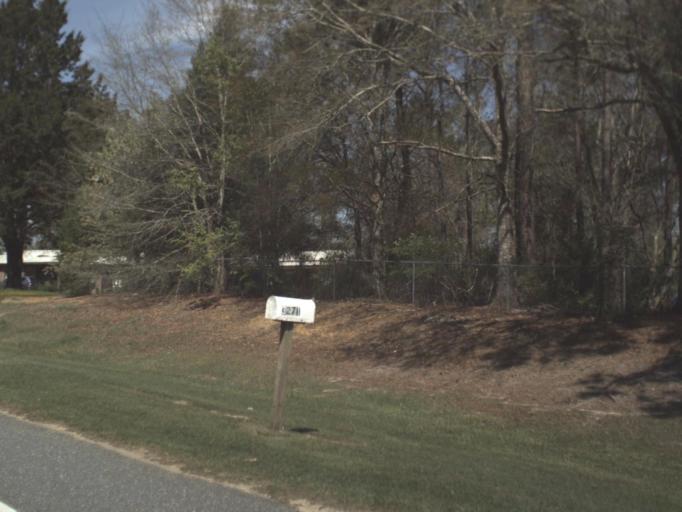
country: US
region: Florida
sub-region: Holmes County
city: Bonifay
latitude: 30.7867
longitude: -85.6566
